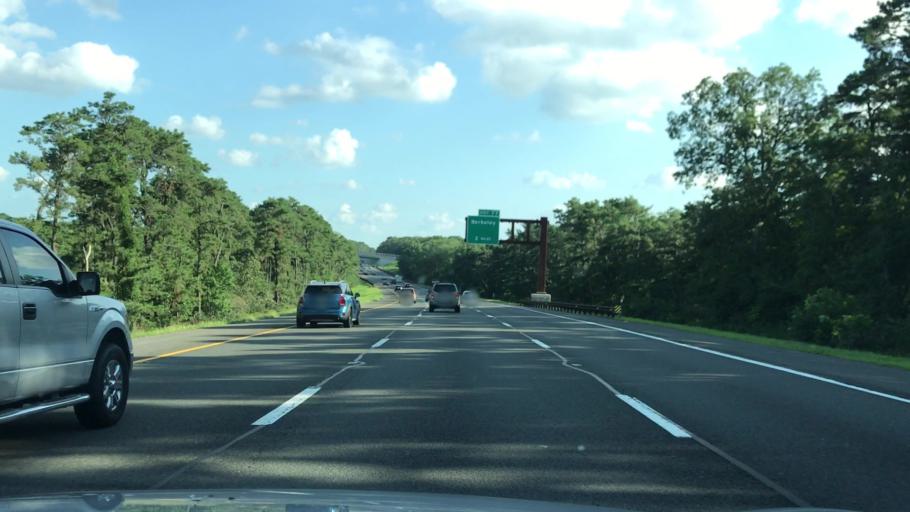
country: US
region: New Jersey
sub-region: Ocean County
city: South Toms River
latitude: 39.9389
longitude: -74.2095
